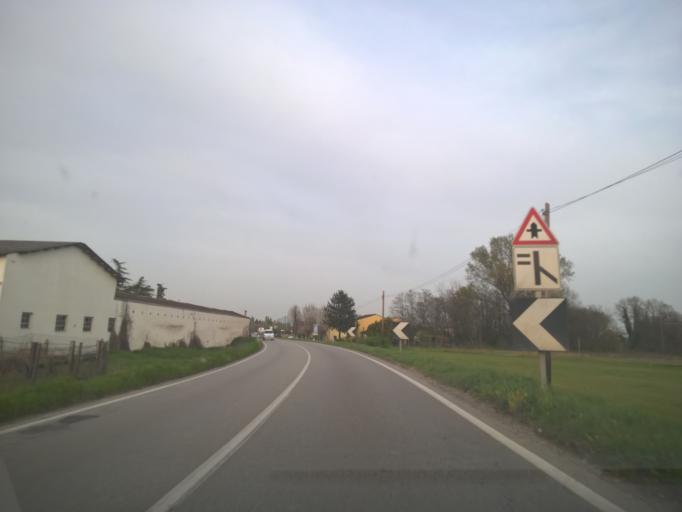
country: IT
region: Veneto
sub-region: Provincia di Padova
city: Megliadino San Fidenzio
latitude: 45.2235
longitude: 11.5051
